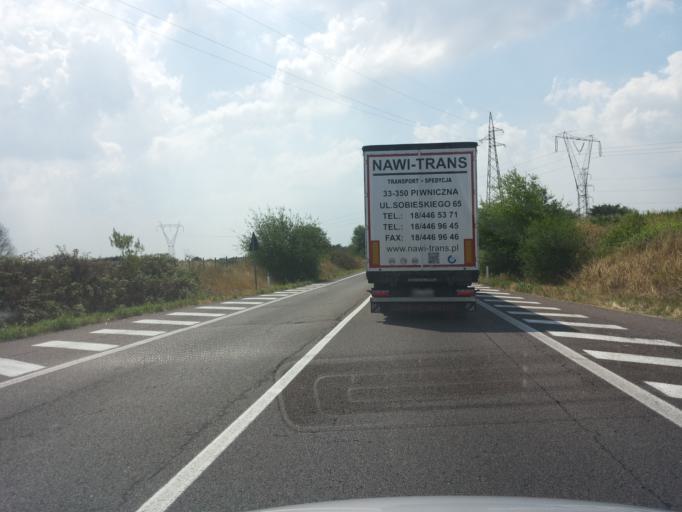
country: IT
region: Veneto
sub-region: Provincia di Verona
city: Cavalcaselle
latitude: 45.4296
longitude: 10.7376
